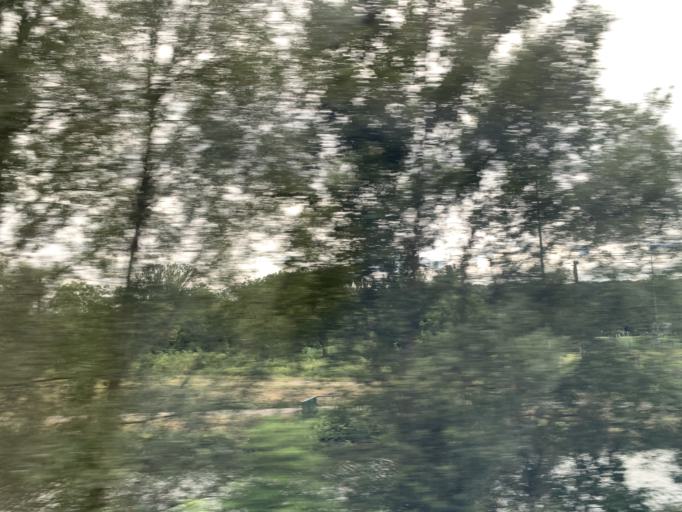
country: FR
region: Alsace
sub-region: Departement du Haut-Rhin
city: Brunstatt
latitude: 47.7219
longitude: 7.3154
